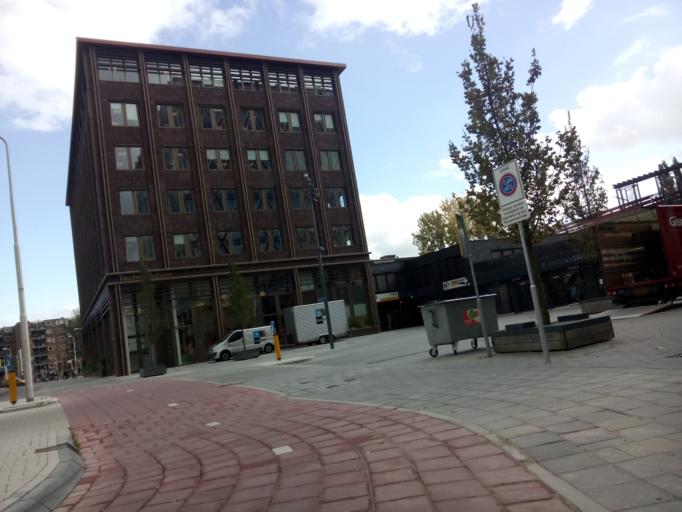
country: NL
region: South Holland
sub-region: Gemeente Gouda
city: Gouda
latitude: 52.0183
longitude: 4.7075
